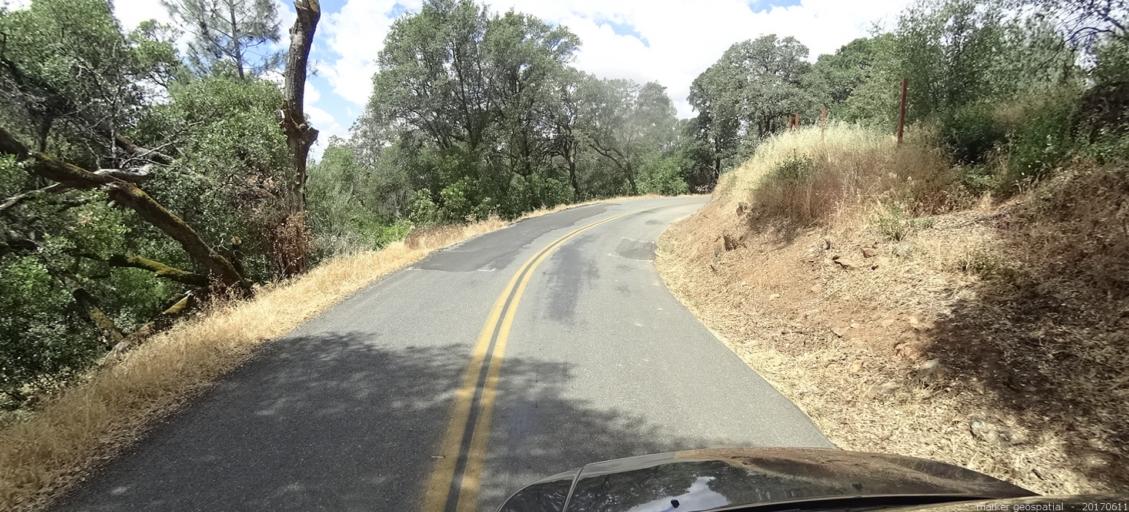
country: US
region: California
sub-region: Butte County
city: Oroville
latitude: 39.6429
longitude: -121.5446
